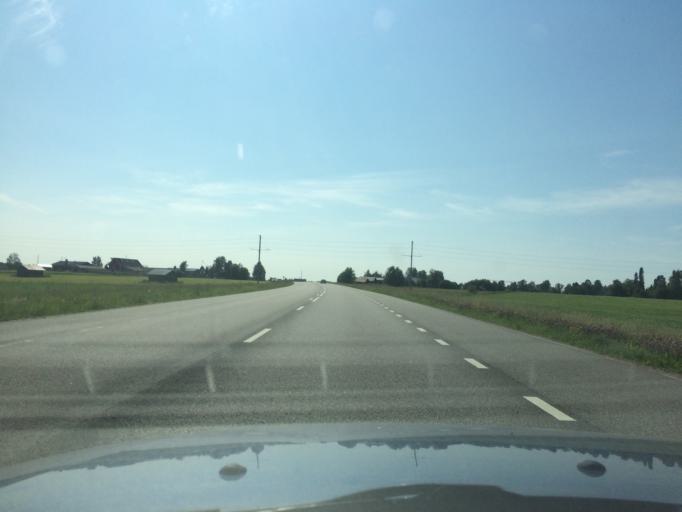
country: SE
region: Norrbotten
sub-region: Pitea Kommun
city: Bergsviken
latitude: 65.3600
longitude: 21.4032
